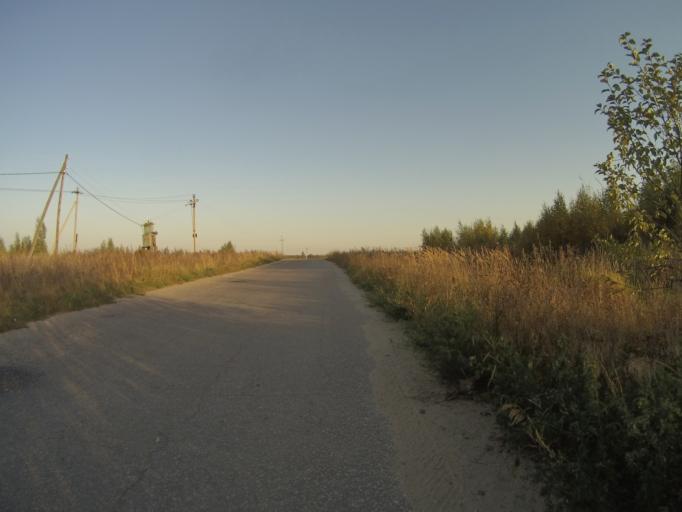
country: RU
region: Vladimir
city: Golovino
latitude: 55.9642
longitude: 40.4552
